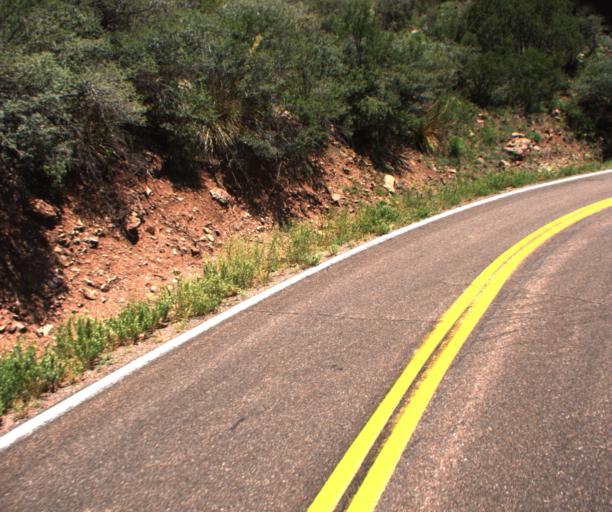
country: US
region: Arizona
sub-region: Greenlee County
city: Morenci
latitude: 33.2141
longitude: -109.3775
